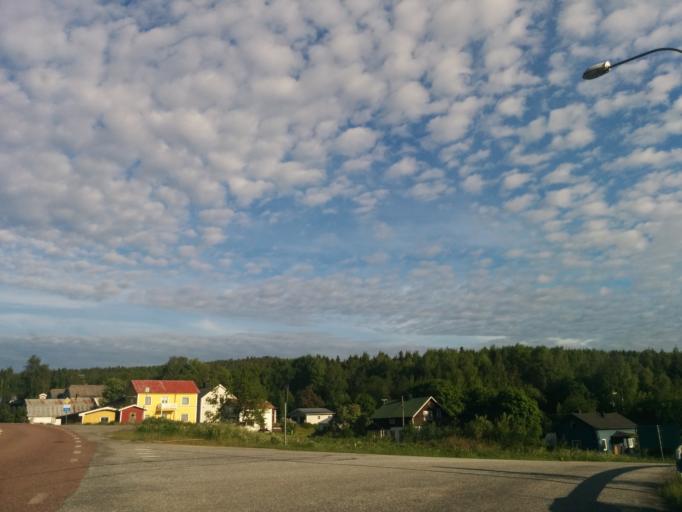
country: SE
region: Vaesternorrland
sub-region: Kramfors Kommun
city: Kramfors
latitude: 62.9230
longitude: 17.9249
